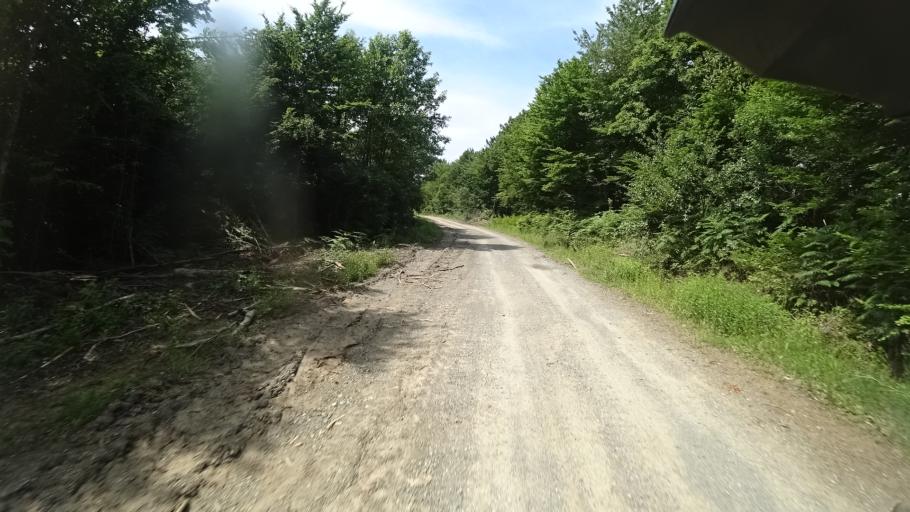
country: HR
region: Sisacko-Moslavacka
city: Gvozd
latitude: 45.3284
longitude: 15.8292
